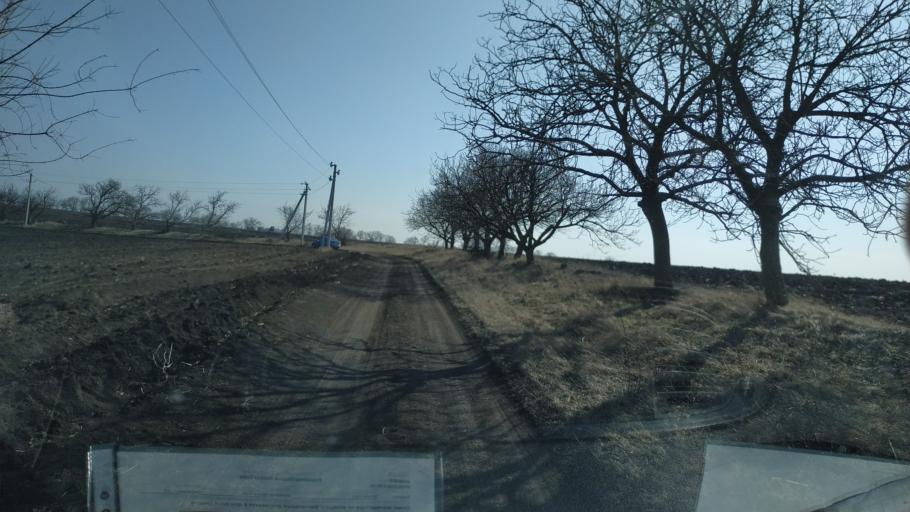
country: MD
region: Causeni
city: Causeni
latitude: 46.5543
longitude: 29.2715
